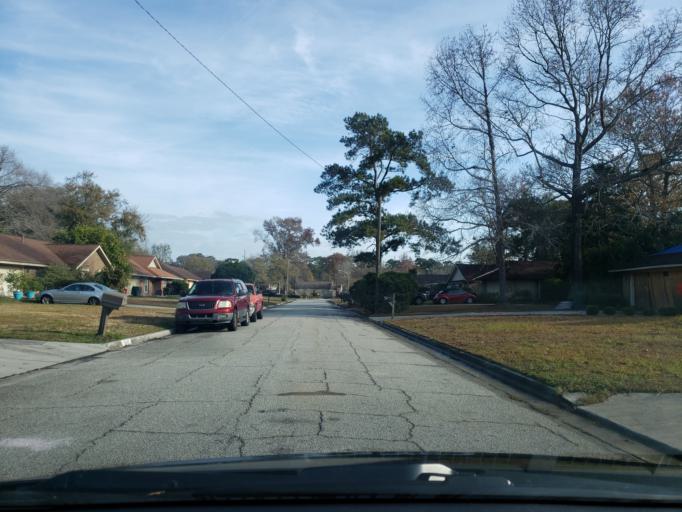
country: US
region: Georgia
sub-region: Chatham County
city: Montgomery
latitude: 31.9999
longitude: -81.1430
